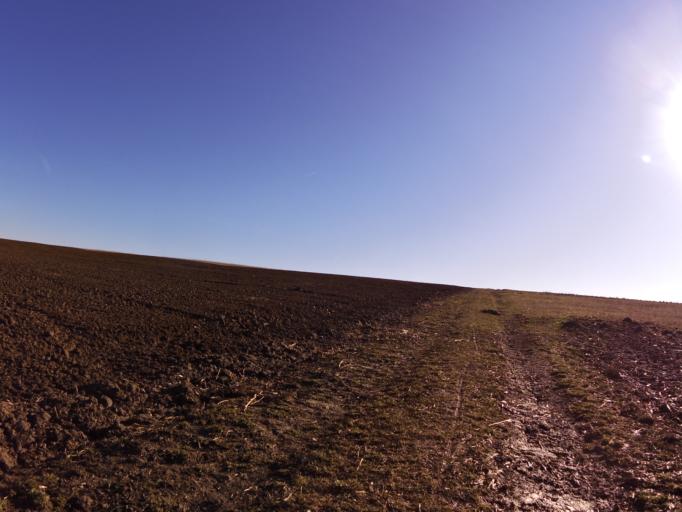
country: DE
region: Bavaria
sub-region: Regierungsbezirk Unterfranken
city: Estenfeld
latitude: 49.8488
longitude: 9.9903
